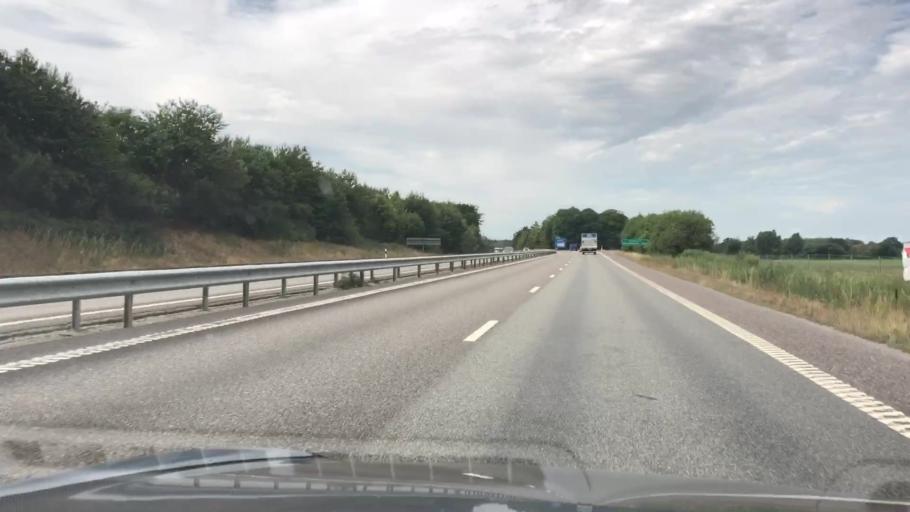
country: SE
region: Blekinge
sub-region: Solvesborgs Kommun
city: Soelvesborg
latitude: 56.0655
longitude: 14.5820
